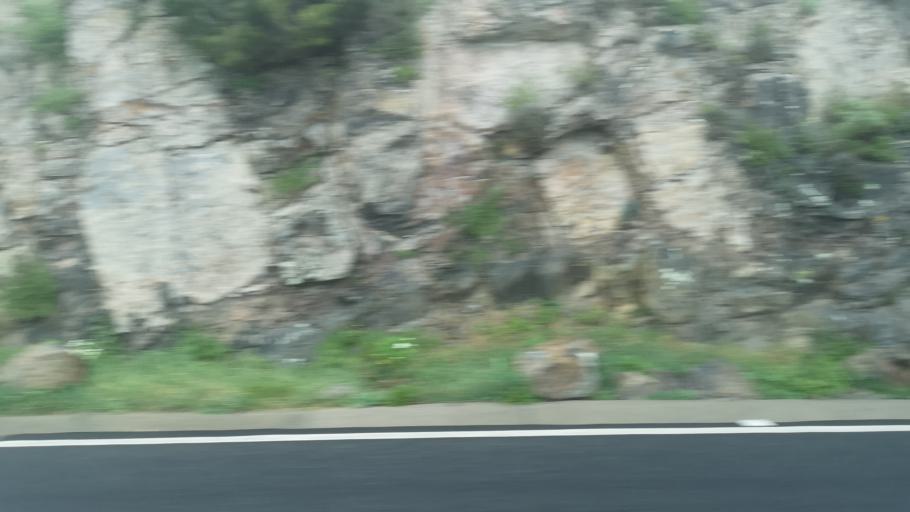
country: ES
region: Canary Islands
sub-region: Provincia de Santa Cruz de Tenerife
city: Alajero
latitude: 28.0999
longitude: -17.2064
